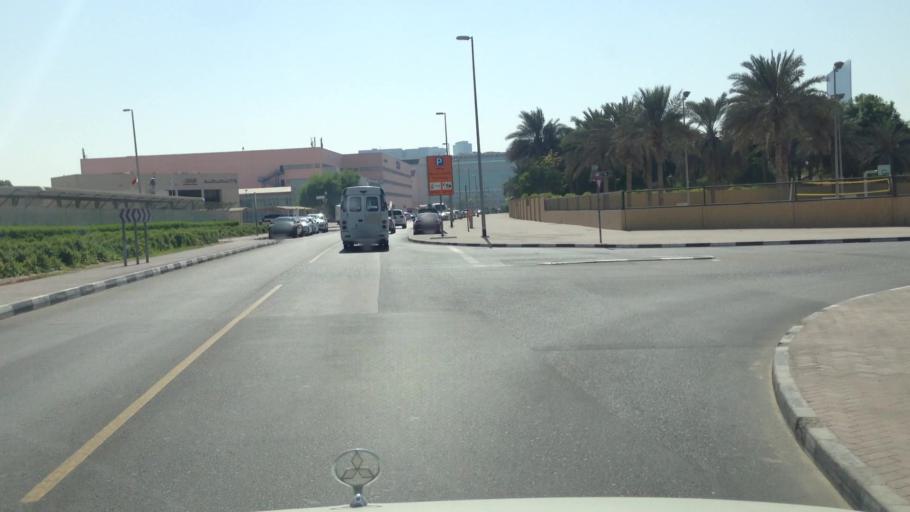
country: AE
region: Ash Shariqah
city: Sharjah
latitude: 25.2410
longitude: 55.3596
